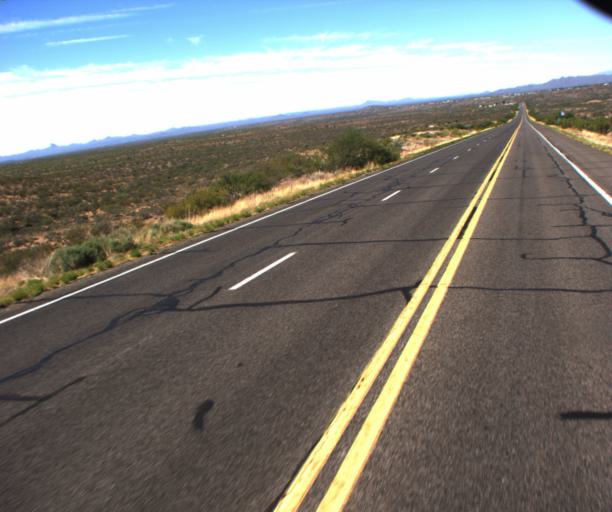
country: US
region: Arizona
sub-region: Yavapai County
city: Congress
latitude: 34.1966
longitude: -112.8117
